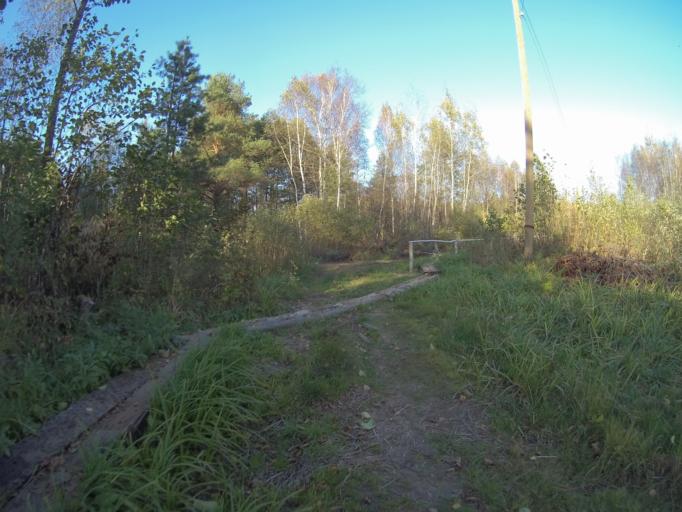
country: RU
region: Vladimir
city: Golovino
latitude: 55.9991
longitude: 40.4207
